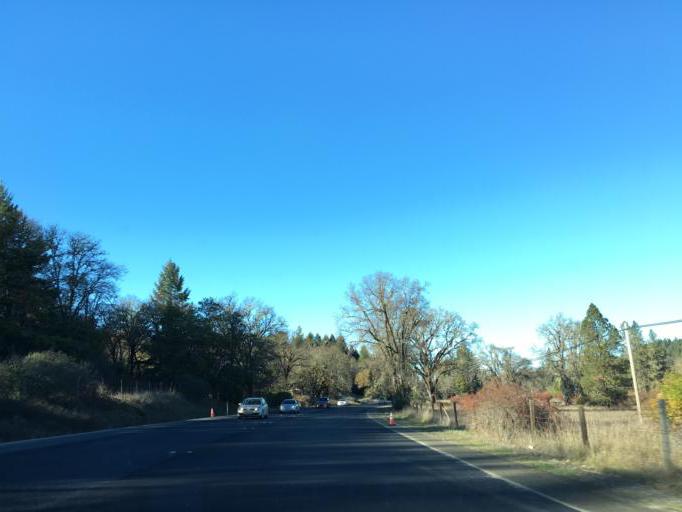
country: US
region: California
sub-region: Mendocino County
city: Laytonville
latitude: 39.6415
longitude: -123.4726
